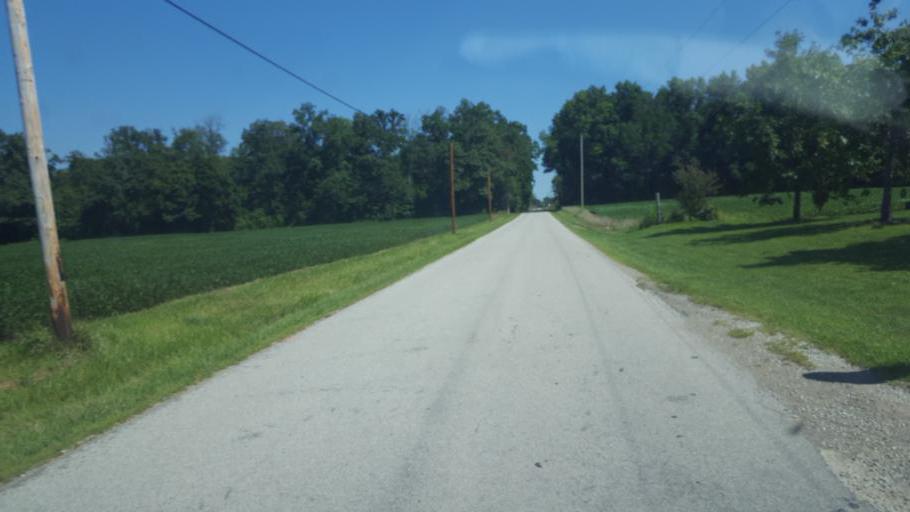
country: US
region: Ohio
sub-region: Morrow County
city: Cardington
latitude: 40.4462
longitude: -82.8964
